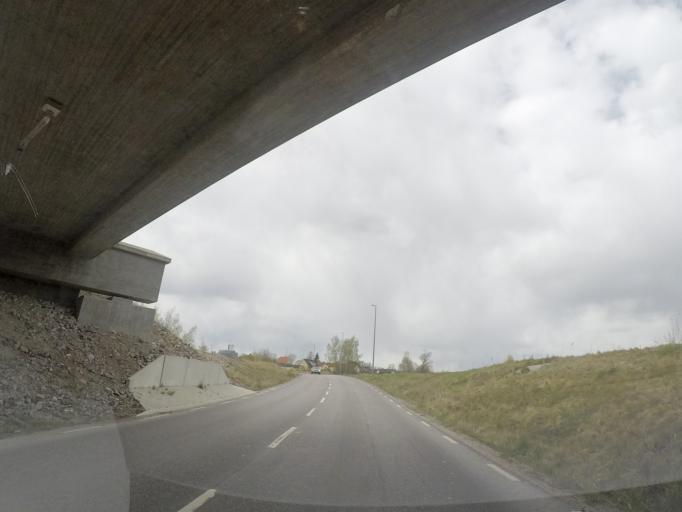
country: SE
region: Soedermanland
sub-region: Nykopings Kommun
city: Stigtomta
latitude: 58.7460
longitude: 16.7314
